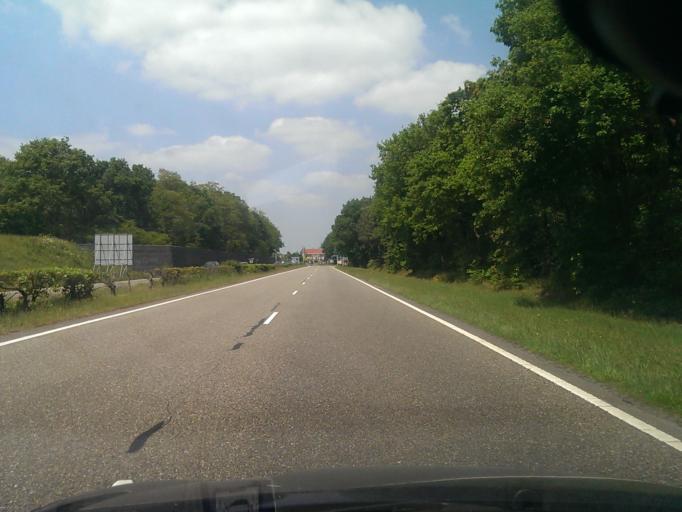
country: NL
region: North Brabant
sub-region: Gemeente Eindhoven
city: Lakerlopen
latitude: 51.4117
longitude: 5.4997
